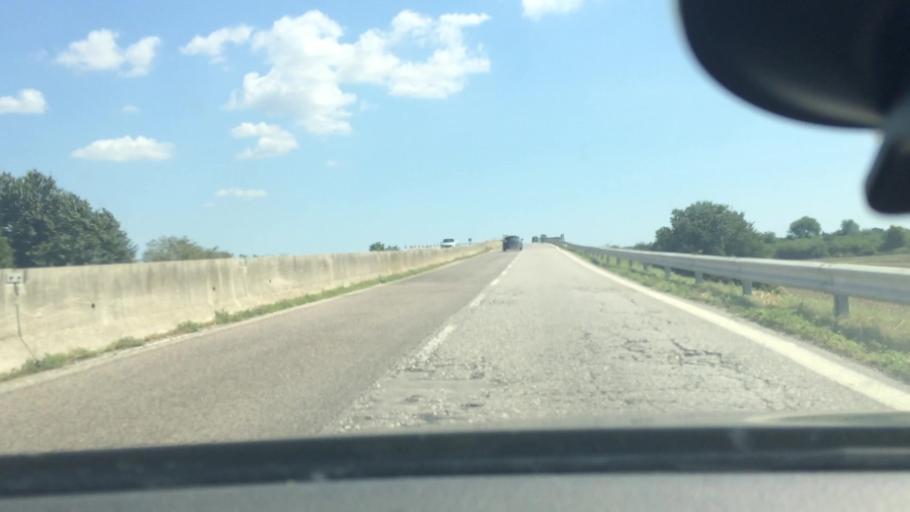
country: IT
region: Emilia-Romagna
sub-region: Provincia di Ferrara
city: Ostellato
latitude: 44.7557
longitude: 11.9509
